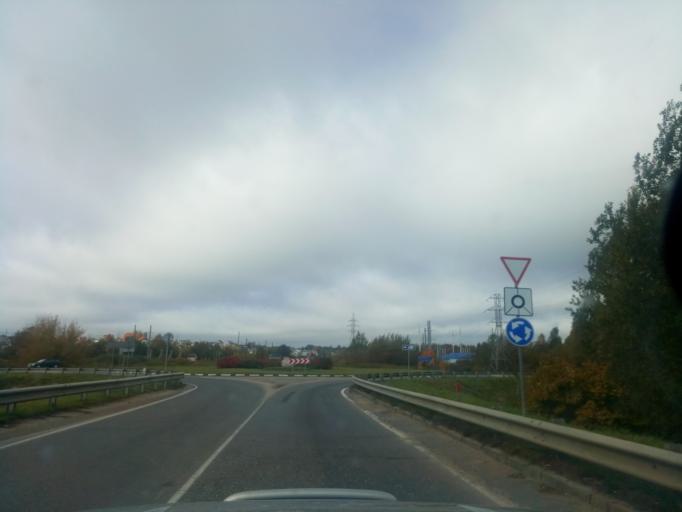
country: BY
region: Minsk
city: Zaslawye
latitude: 54.0004
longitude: 27.2784
